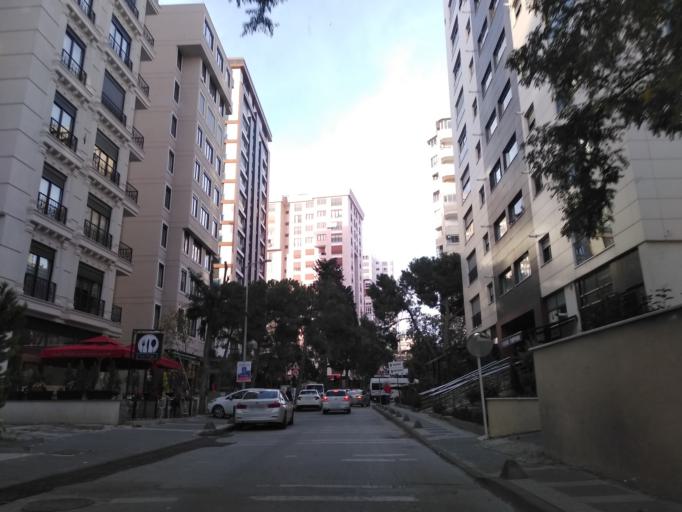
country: TR
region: Istanbul
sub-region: Atasehir
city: Atasehir
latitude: 40.9678
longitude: 29.0881
